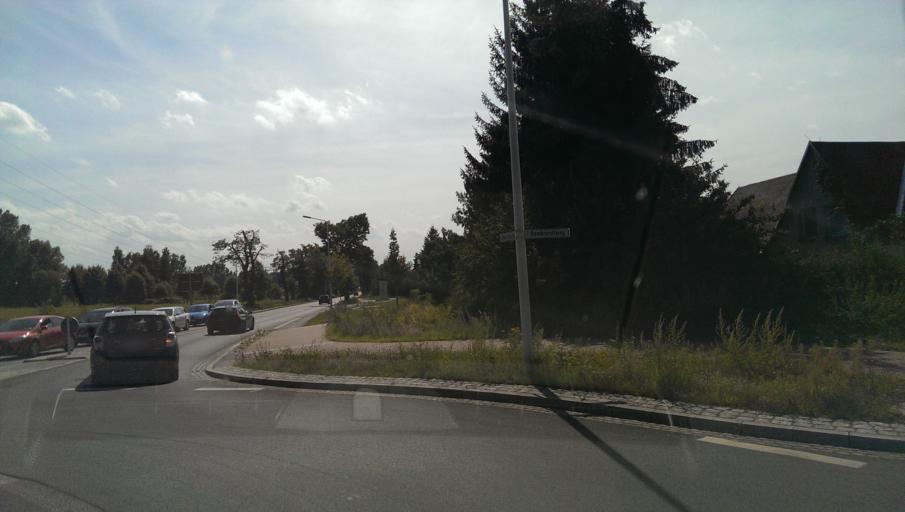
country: DE
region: Saxony-Anhalt
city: Wittenburg
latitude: 51.8866
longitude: 12.6601
